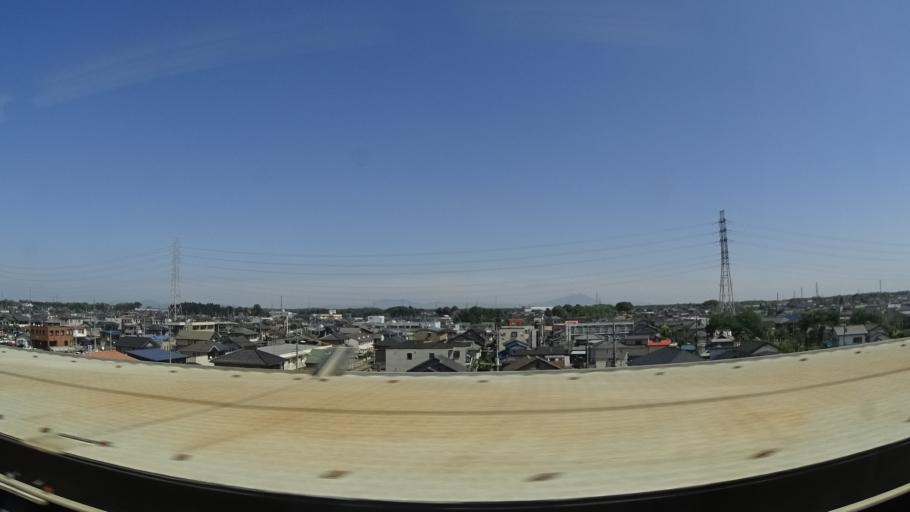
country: JP
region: Tochigi
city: Mibu
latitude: 36.3738
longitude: 139.8417
